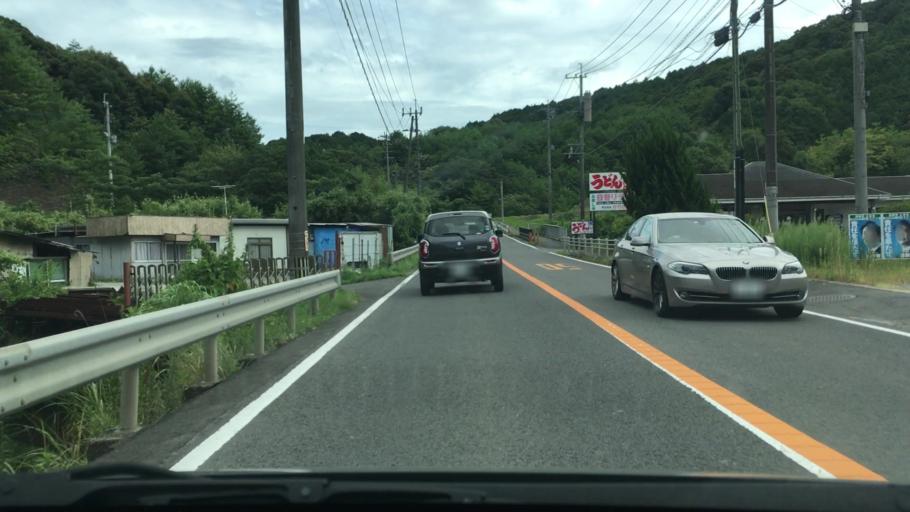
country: JP
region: Nagasaki
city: Sasebo
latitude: 32.9950
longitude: 129.7330
